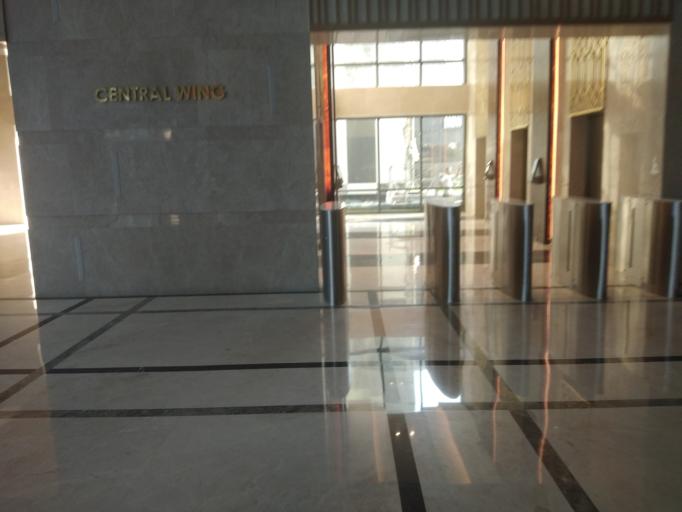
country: IN
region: Maharashtra
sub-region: Mumbai Suburban
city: Powai
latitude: 19.1521
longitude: 72.8548
